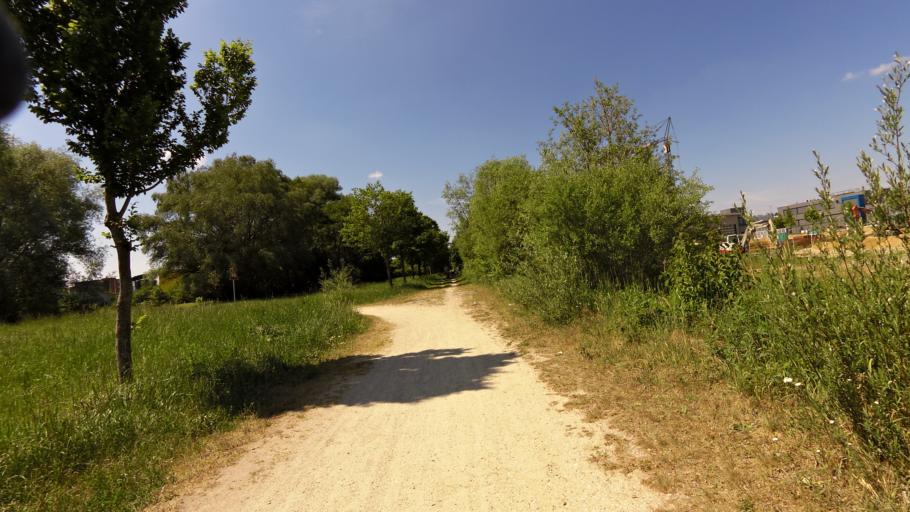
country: DE
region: Bavaria
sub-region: Lower Bavaria
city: Tiefenbach
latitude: 48.5421
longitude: 12.0997
